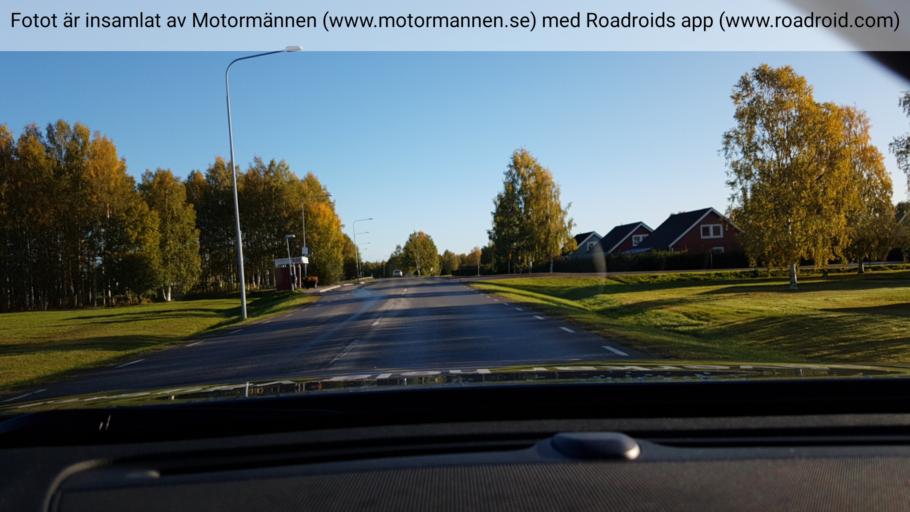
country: SE
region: Norrbotten
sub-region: Lulea Kommun
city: Sodra Sunderbyn
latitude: 65.6581
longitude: 21.9474
